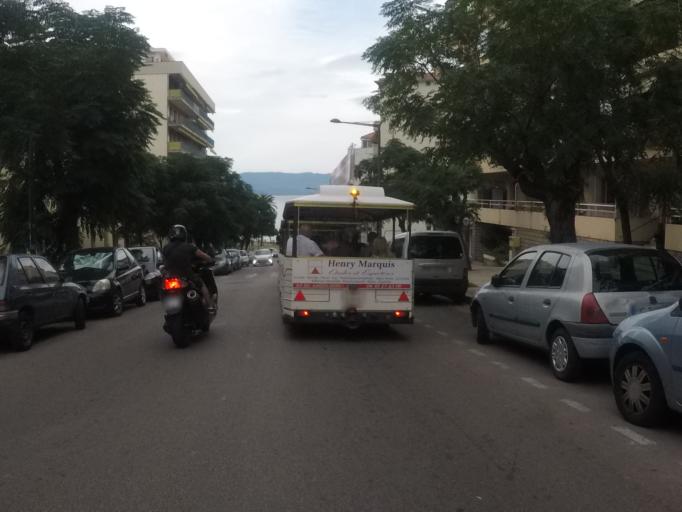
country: FR
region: Corsica
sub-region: Departement de la Corse-du-Sud
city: Ajaccio
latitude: 41.9141
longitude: 8.7250
